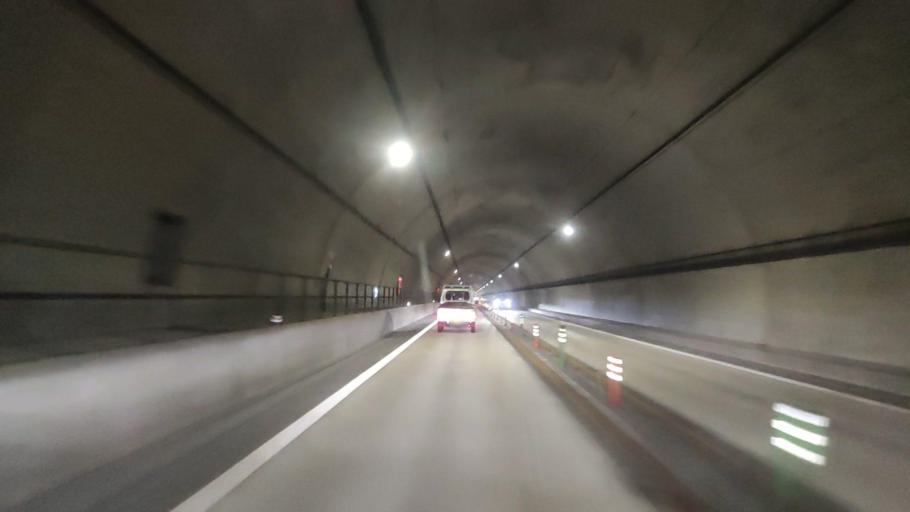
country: JP
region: Wakayama
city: Tanabe
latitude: 33.6254
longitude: 135.4172
